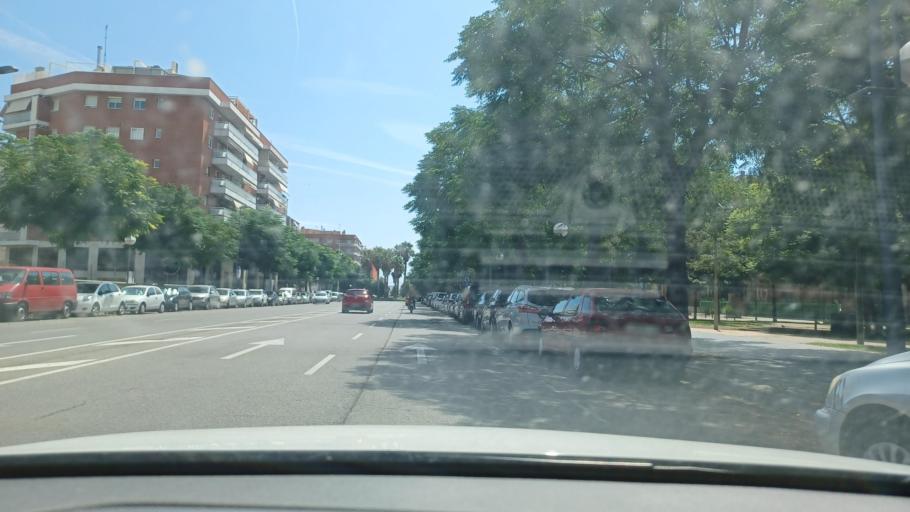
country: ES
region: Catalonia
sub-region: Provincia de Tarragona
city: Tarragona
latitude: 41.1150
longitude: 1.2406
